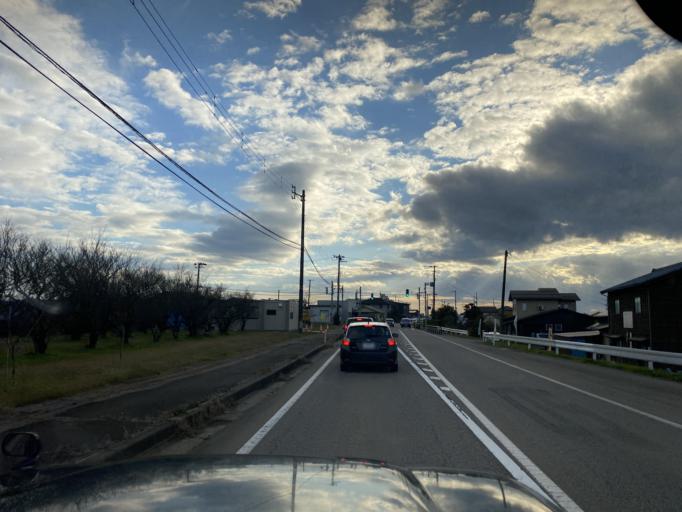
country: JP
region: Niigata
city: Kamo
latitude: 37.6745
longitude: 139.0135
